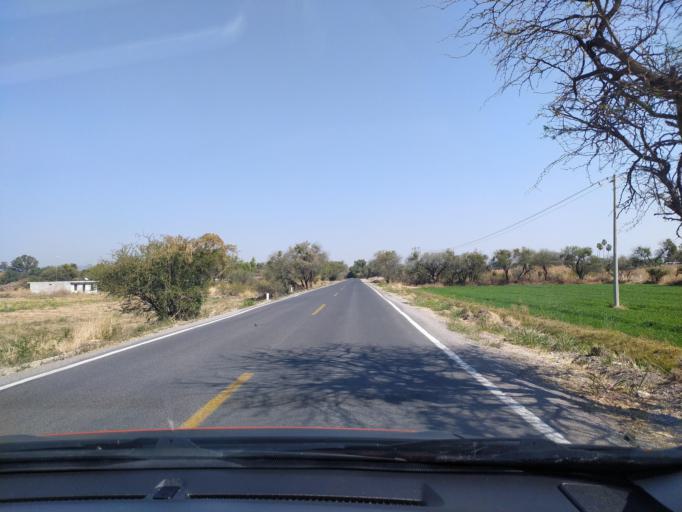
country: MX
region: Guanajuato
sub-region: San Francisco del Rincon
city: San Ignacio de Hidalgo
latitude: 20.8776
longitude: -101.8596
